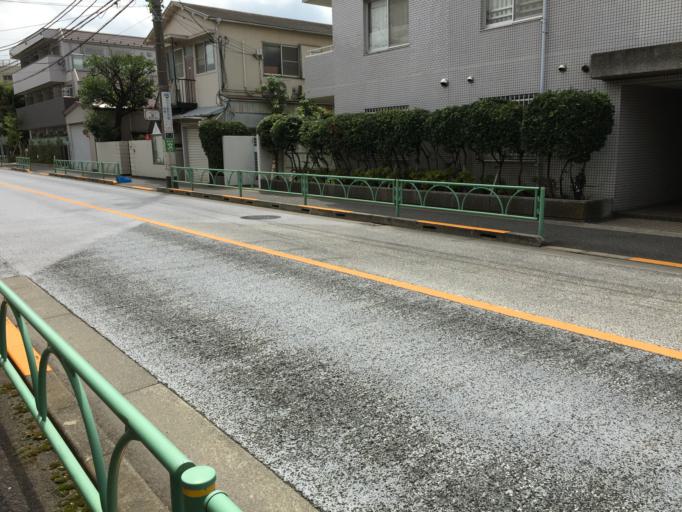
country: JP
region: Tokyo
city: Tokyo
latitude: 35.6544
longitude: 139.6379
